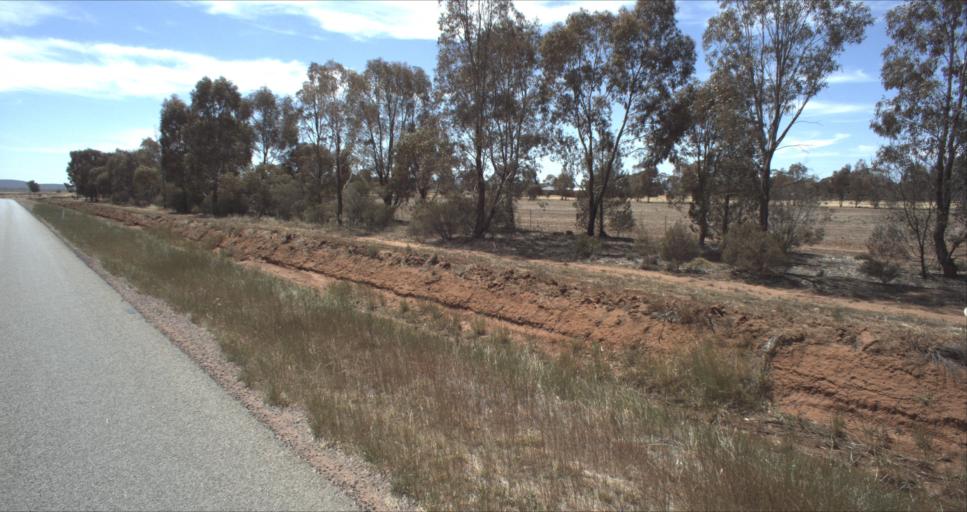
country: AU
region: New South Wales
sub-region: Leeton
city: Leeton
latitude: -34.5591
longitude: 146.4532
